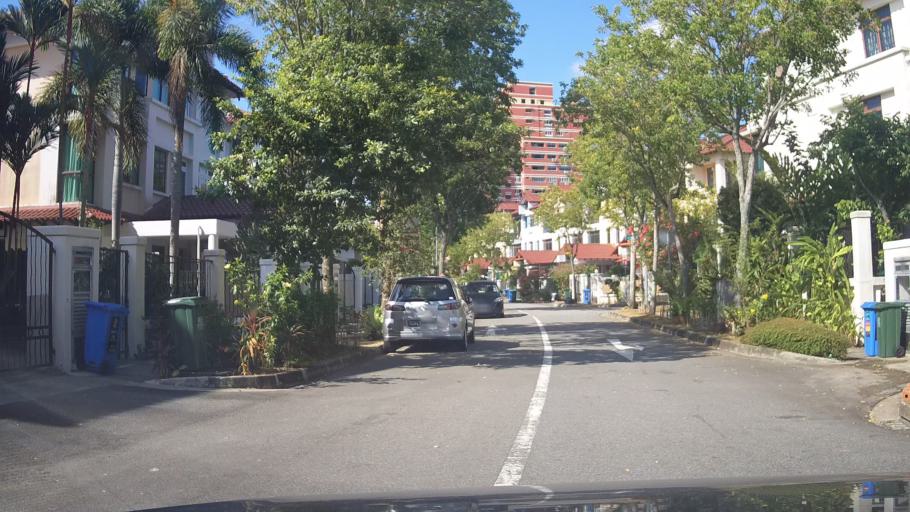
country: MY
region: Johor
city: Kampung Pasir Gudang Baru
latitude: 1.3788
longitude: 103.9452
